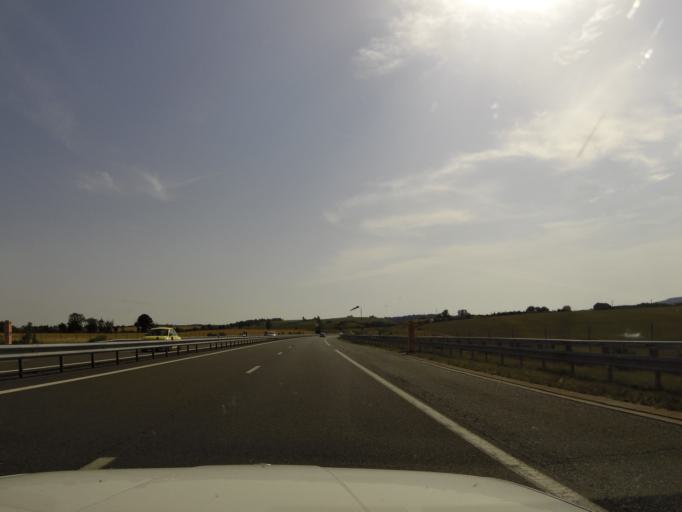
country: FR
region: Midi-Pyrenees
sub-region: Departement de l'Aveyron
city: Severac-le-Chateau
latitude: 44.2662
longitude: 3.0796
